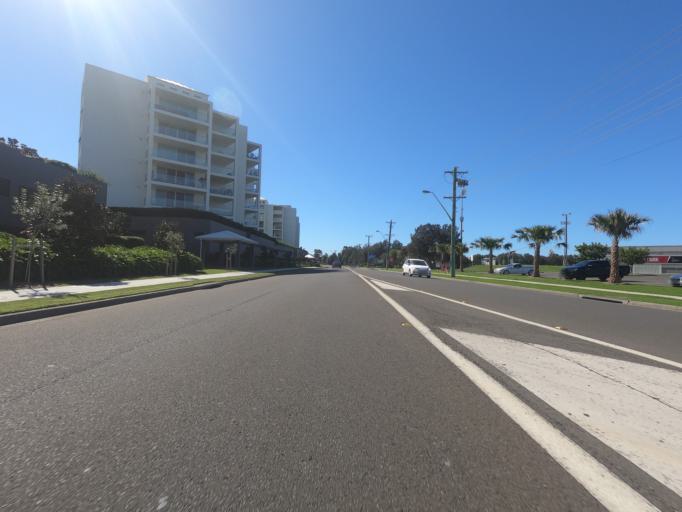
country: AU
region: New South Wales
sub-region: Wollongong
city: Fairy Meadow
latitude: -34.3908
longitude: 150.9030
